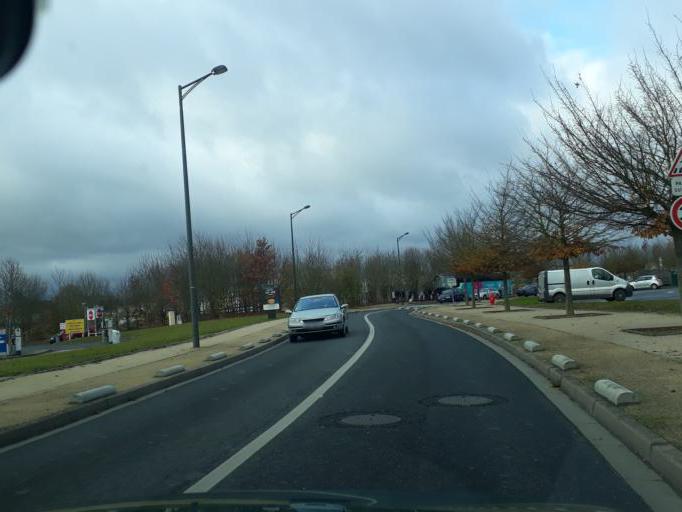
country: FR
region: Centre
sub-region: Departement du Loir-et-Cher
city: Villebarou
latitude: 47.6142
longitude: 1.3252
